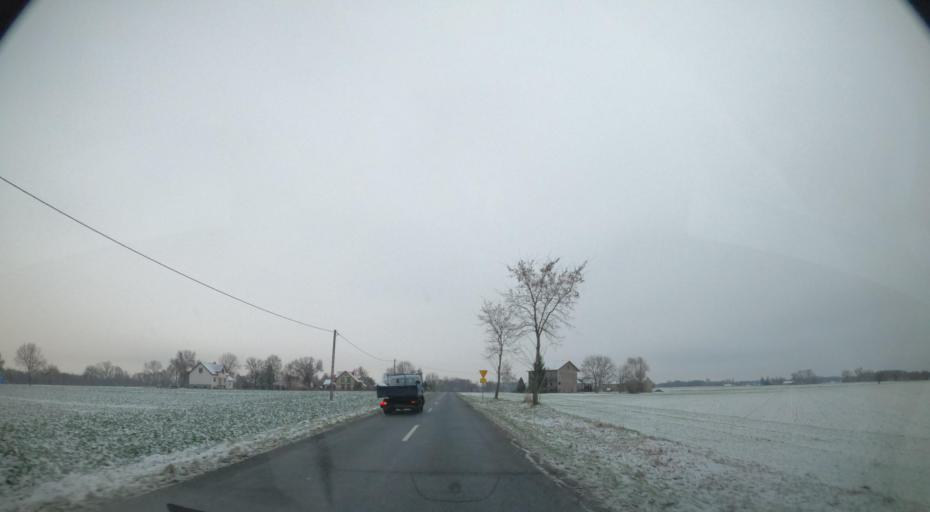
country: PL
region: Kujawsko-Pomorskie
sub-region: Powiat lipnowski
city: Dobrzyn nad Wisla
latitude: 52.6542
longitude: 19.3949
